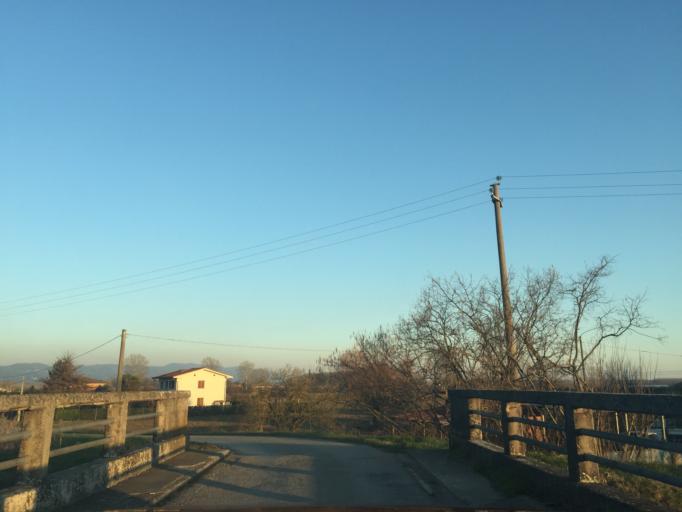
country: IT
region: Tuscany
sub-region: Provincia di Pistoia
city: Anchione
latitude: 43.8271
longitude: 10.7652
